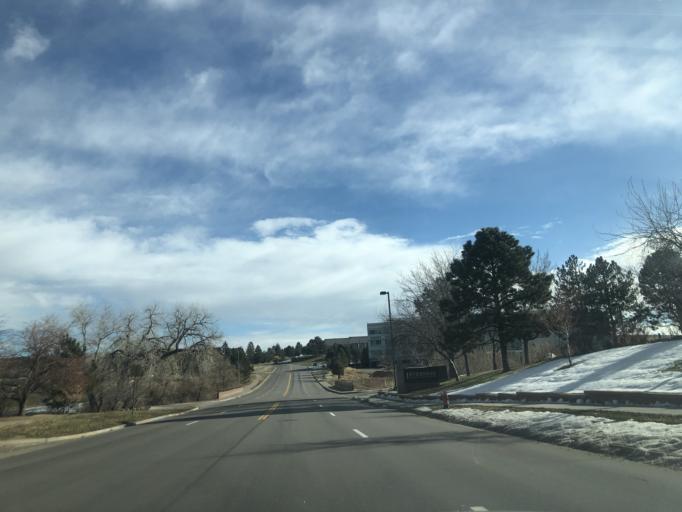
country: US
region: Colorado
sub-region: Douglas County
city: Meridian
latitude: 39.5597
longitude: -104.8632
